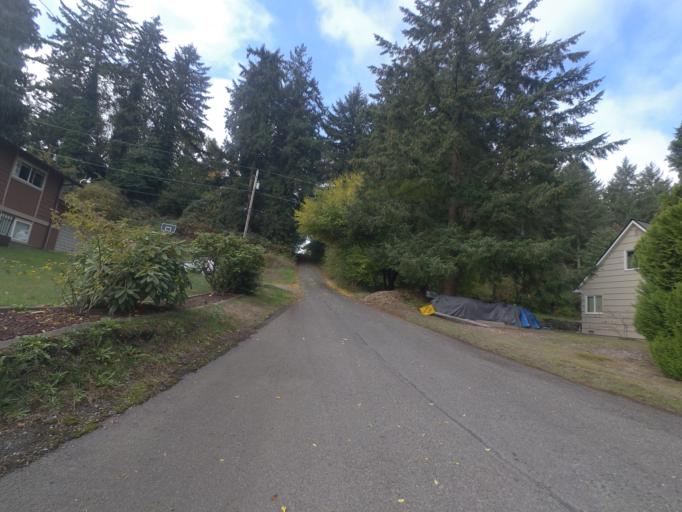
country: US
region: Washington
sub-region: Pierce County
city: Lakewood
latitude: 47.2012
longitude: -122.5035
